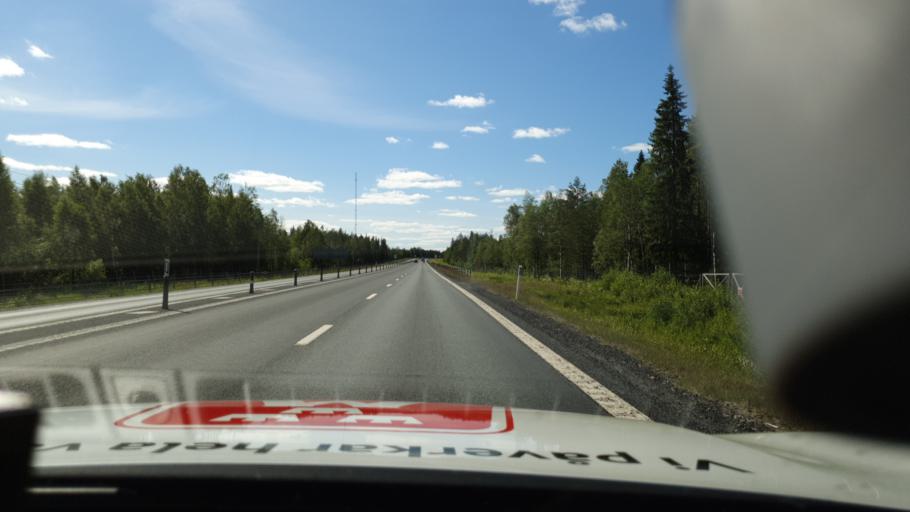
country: SE
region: Norrbotten
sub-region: Haparanda Kommun
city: Haparanda
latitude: 65.8116
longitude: 23.9056
